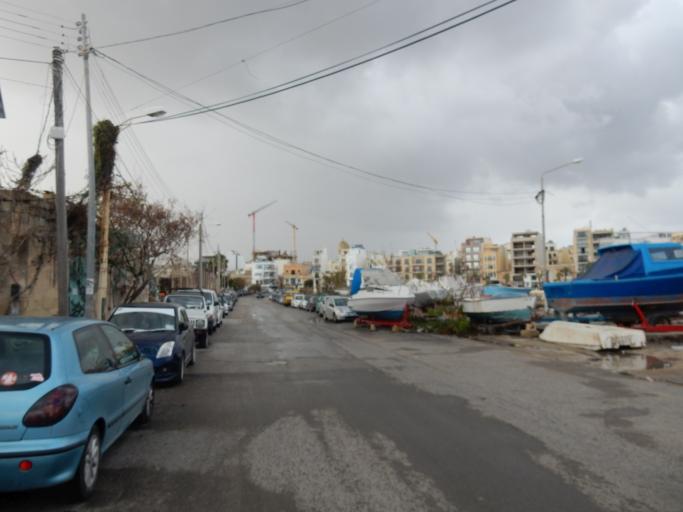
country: MT
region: Ta' Xbiex
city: Ta' Xbiex
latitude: 35.9043
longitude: 14.4983
